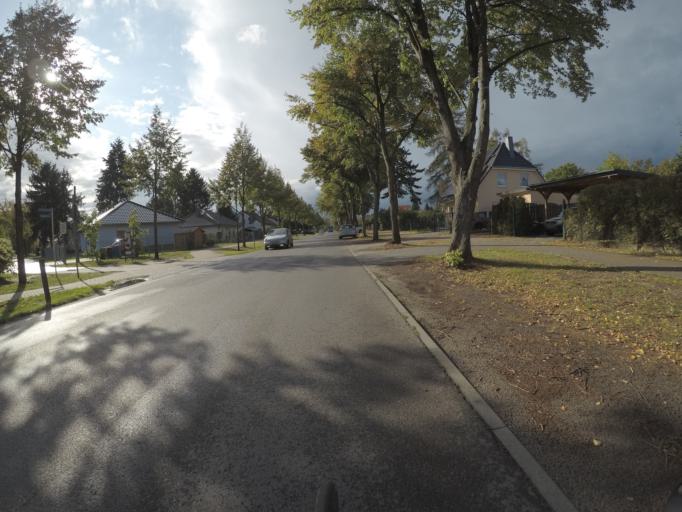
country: DE
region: Brandenburg
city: Petershagen
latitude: 52.5152
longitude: 13.7388
